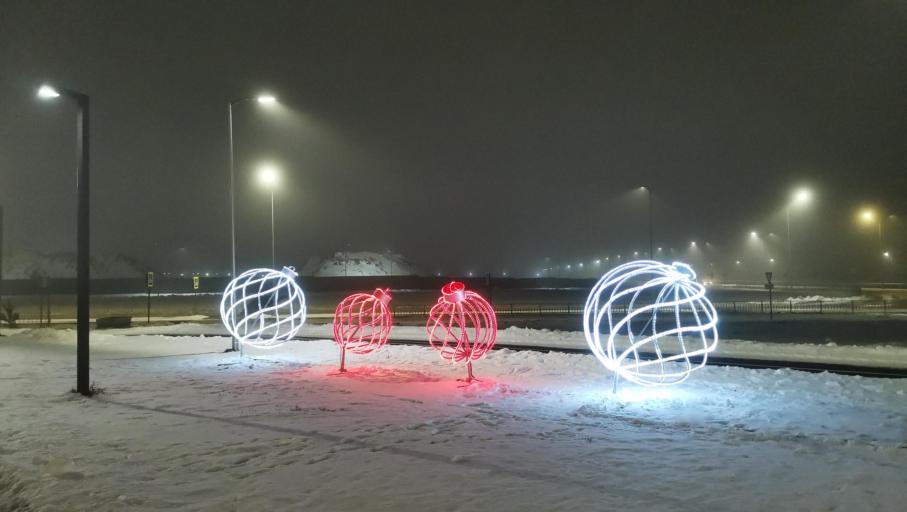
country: RU
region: Tatarstan
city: Sviyazhsk
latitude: 55.7472
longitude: 48.7406
